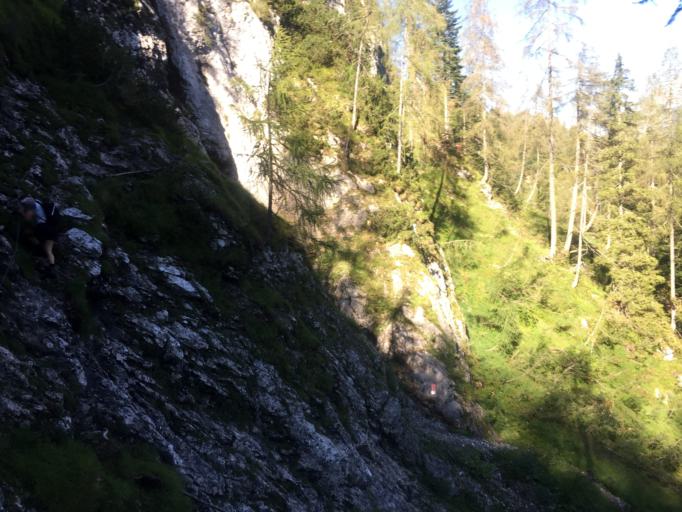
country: IT
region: Veneto
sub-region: Provincia di Belluno
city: Granvilla
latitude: 46.5528
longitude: 12.7343
